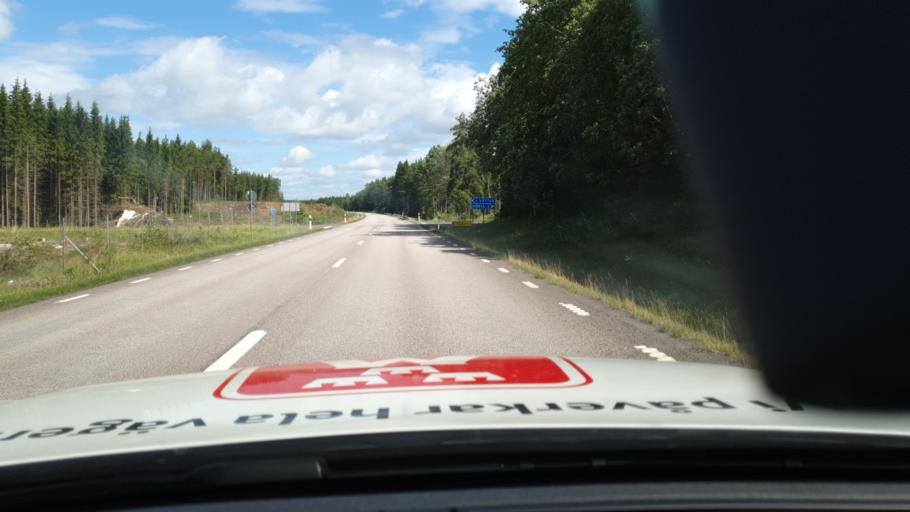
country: SE
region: Vaestra Goetaland
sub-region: Tidaholms Kommun
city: Tidaholm
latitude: 58.0843
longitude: 13.8759
